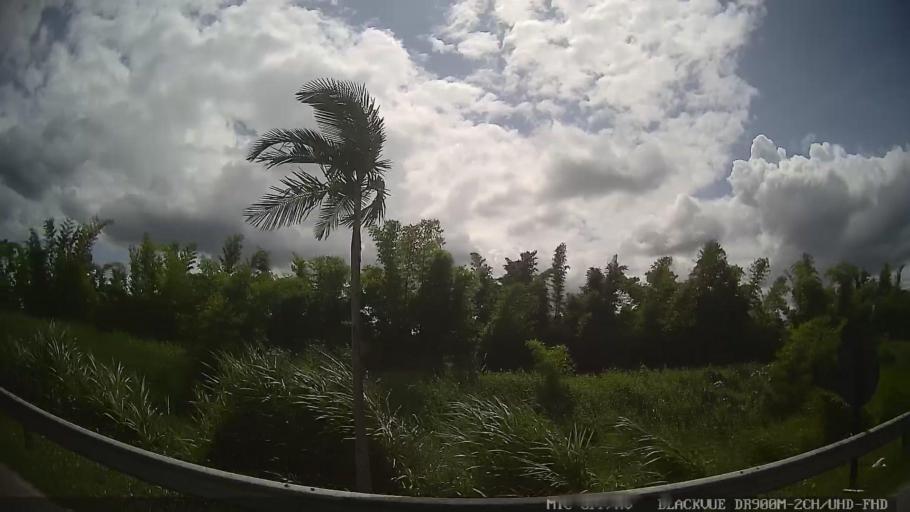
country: BR
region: Sao Paulo
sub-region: Suzano
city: Suzano
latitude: -23.5661
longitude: -46.2556
